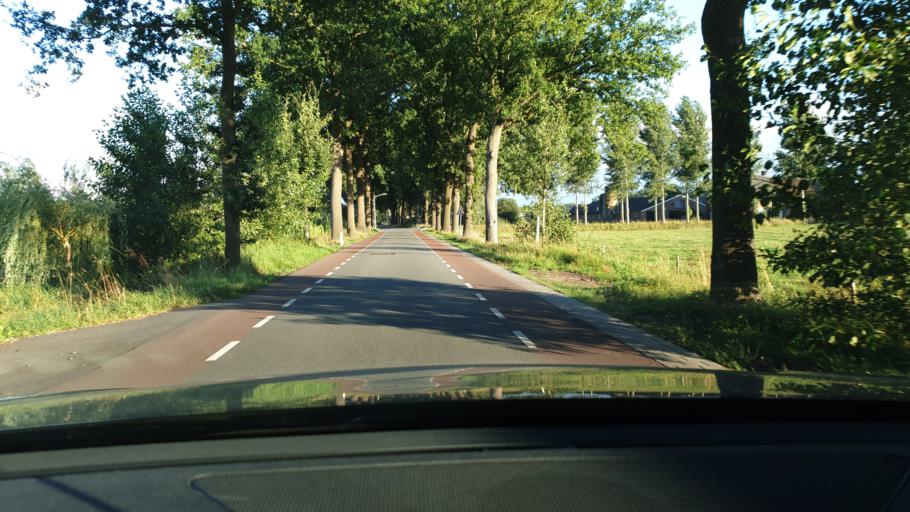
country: NL
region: North Brabant
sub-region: Gemeente Best
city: Best
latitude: 51.5329
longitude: 5.4074
